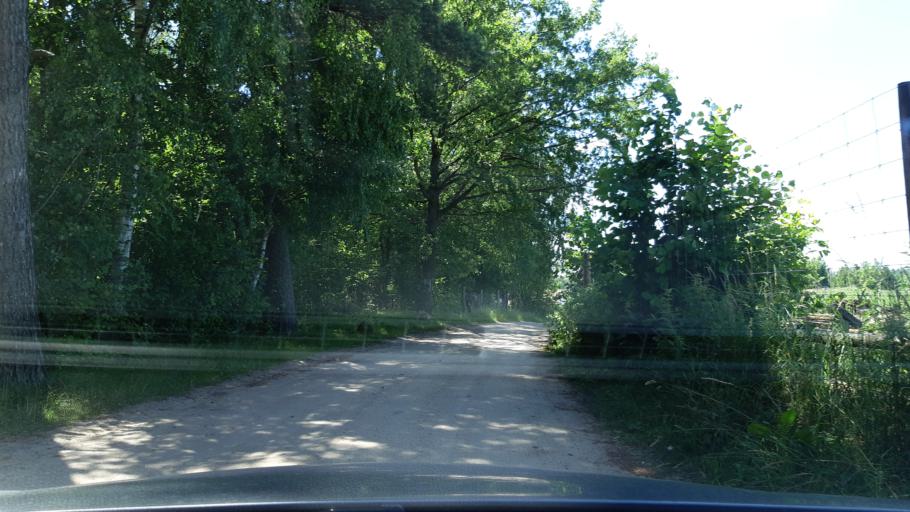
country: PL
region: Warmian-Masurian Voivodeship
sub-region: Powiat piski
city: Ruciane-Nida
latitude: 53.7108
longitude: 21.4889
